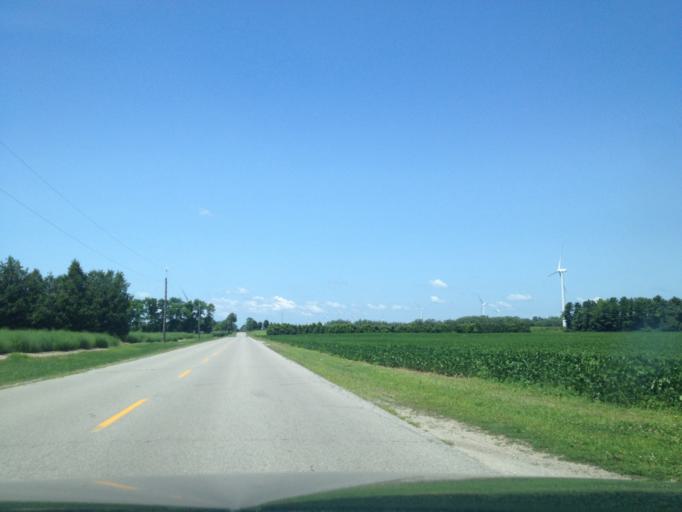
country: CA
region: Ontario
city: Aylmer
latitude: 42.6079
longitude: -80.6803
